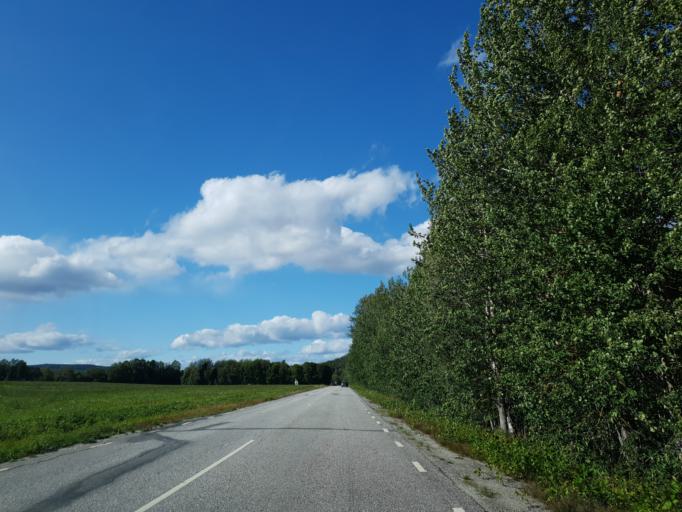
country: SE
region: Vaesternorrland
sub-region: OErnskoeldsviks Kommun
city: Kopmanholmen
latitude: 63.1796
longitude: 18.5372
